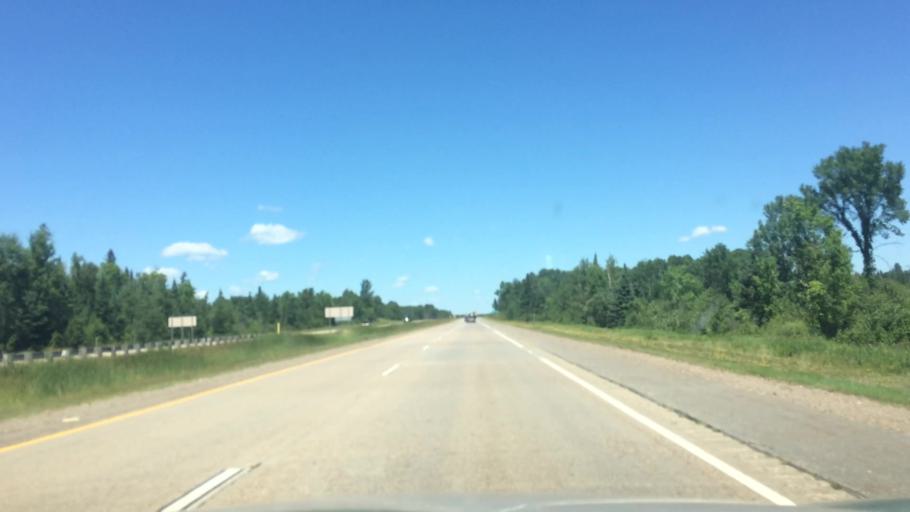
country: US
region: Wisconsin
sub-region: Lincoln County
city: Tomahawk
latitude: 45.3940
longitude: -89.6721
